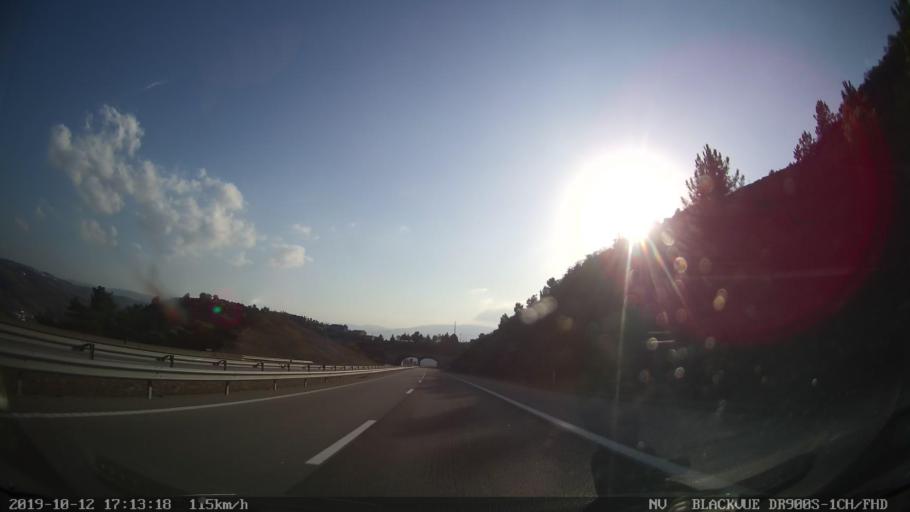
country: PT
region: Vila Real
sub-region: Santa Marta de Penaguiao
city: Santa Marta de Penaguiao
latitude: 41.2076
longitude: -7.7431
